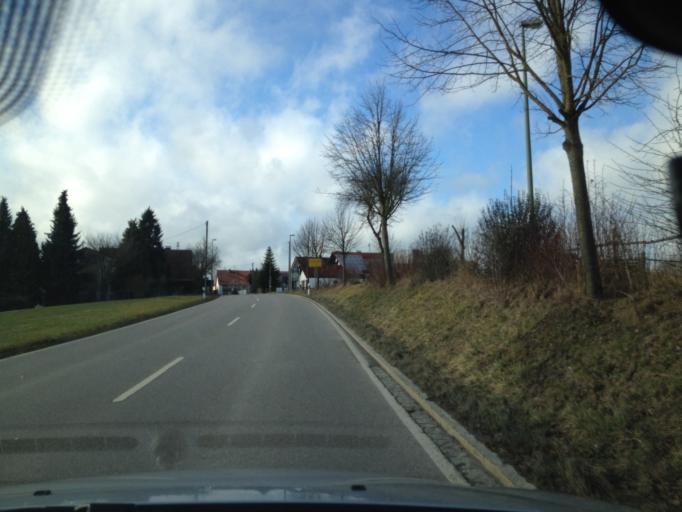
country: DE
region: Bavaria
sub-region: Swabia
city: Grossaitingen
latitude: 48.2592
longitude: 10.7362
